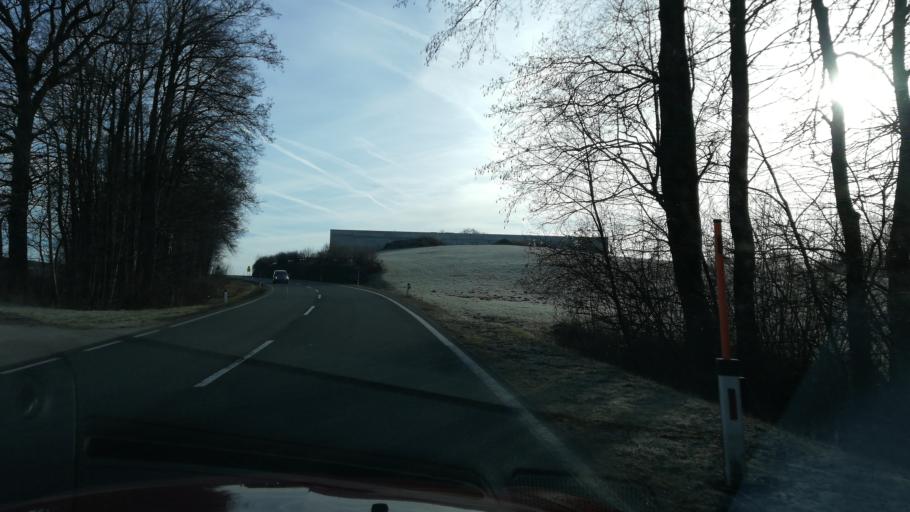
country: AT
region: Upper Austria
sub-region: Politischer Bezirk Steyr-Land
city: Waldneukirchen
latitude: 48.0258
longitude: 14.2405
